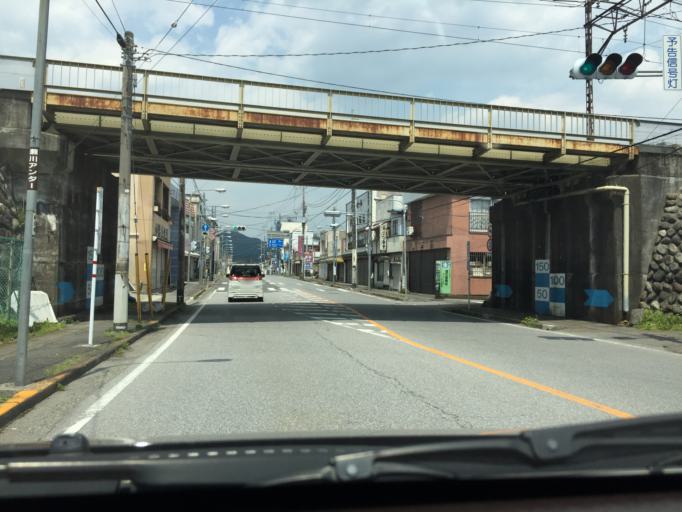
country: JP
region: Tochigi
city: Imaichi
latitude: 36.7271
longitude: 139.6860
